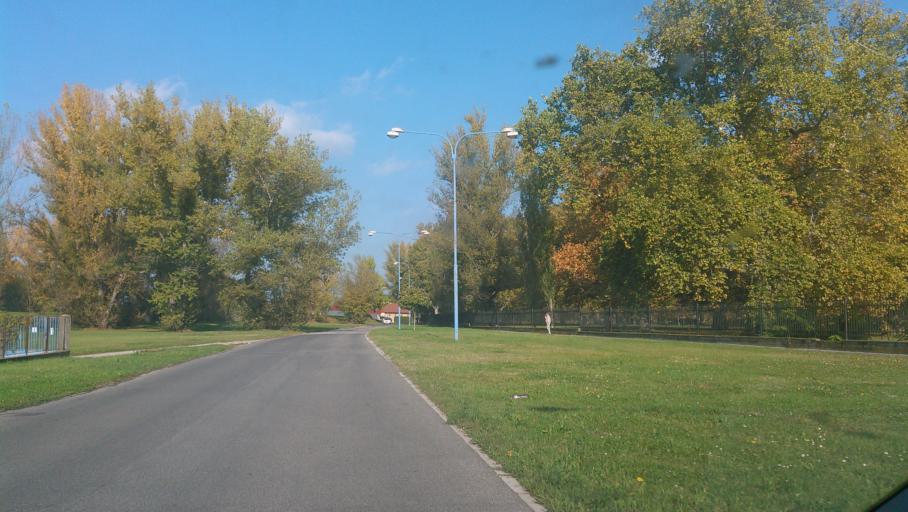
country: SK
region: Trnavsky
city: Hlohovec
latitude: 48.4217
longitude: 17.7841
